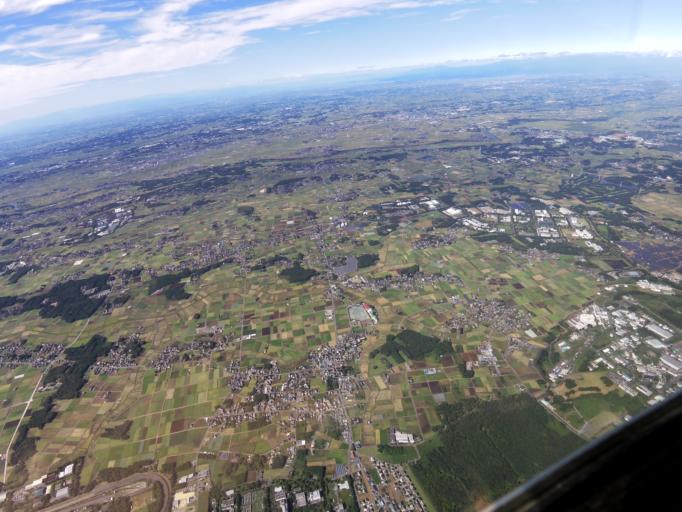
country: JP
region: Ibaraki
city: Tsukuba
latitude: 36.1336
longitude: 140.0818
